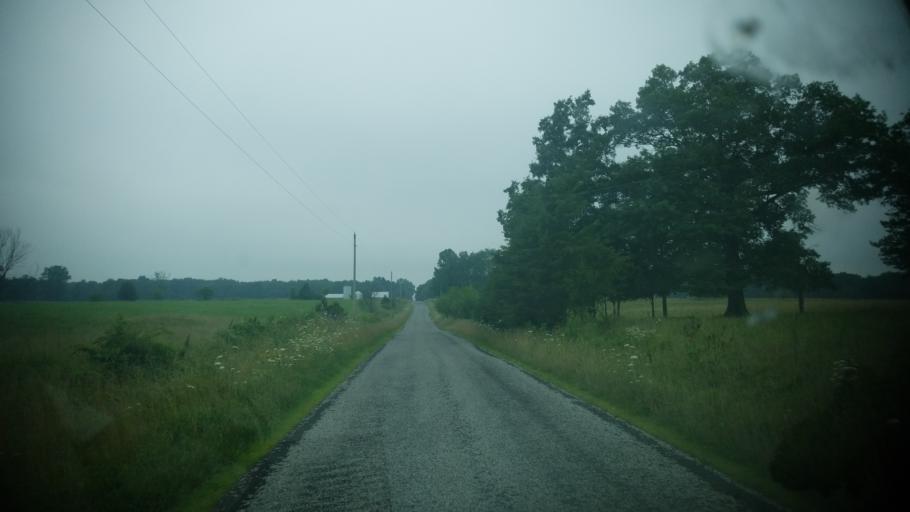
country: US
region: Illinois
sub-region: Clay County
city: Flora
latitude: 38.5735
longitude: -88.3804
